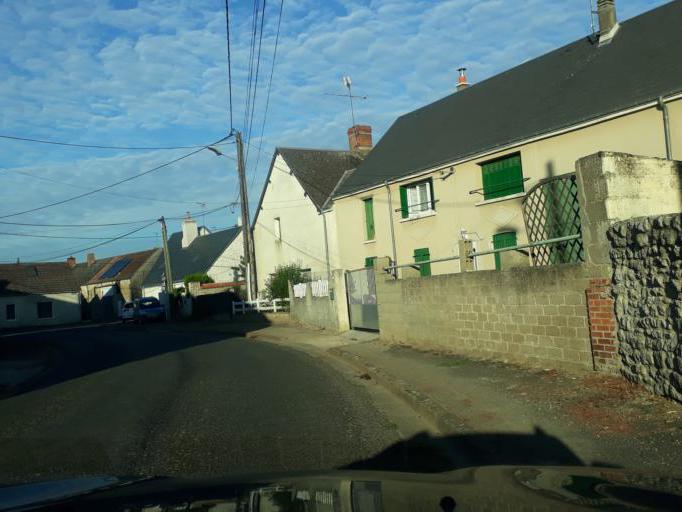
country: FR
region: Centre
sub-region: Departement du Loir-et-Cher
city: Ouzouer-le-Marche
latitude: 47.9691
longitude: 1.5382
